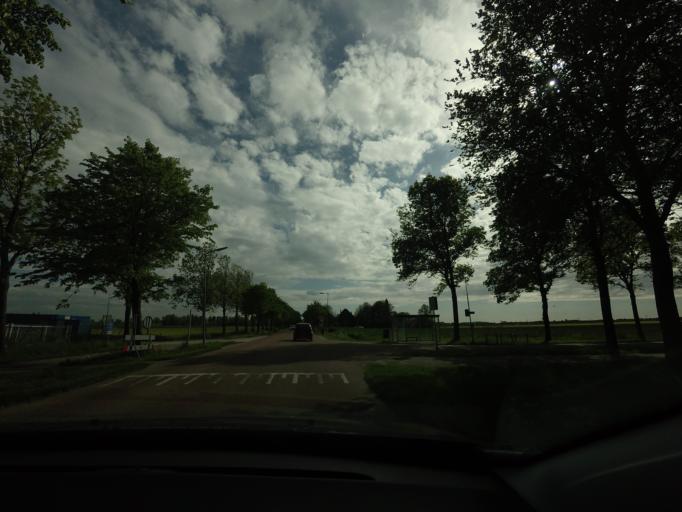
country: NL
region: North Holland
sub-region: Gemeente Beemster
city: Halfweg
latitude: 52.5452
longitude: 4.9108
